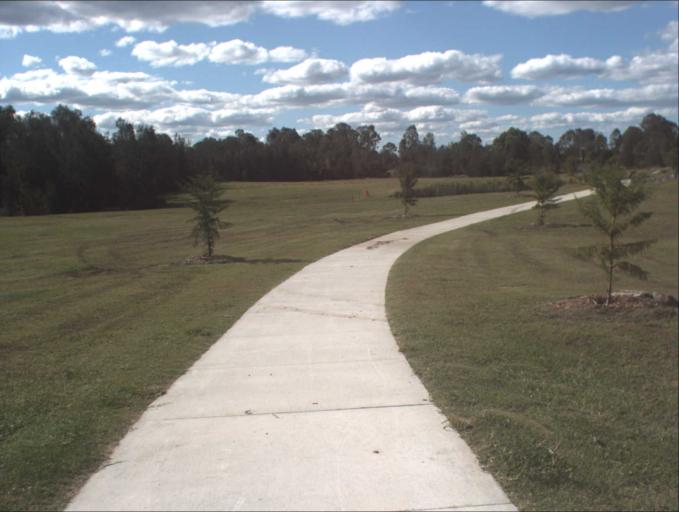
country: AU
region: Queensland
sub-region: Logan
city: Chambers Flat
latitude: -27.7763
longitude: 153.0972
